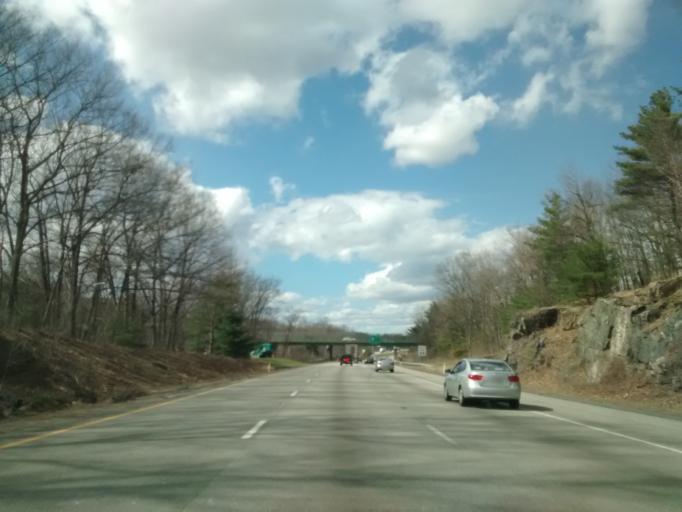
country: US
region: Massachusetts
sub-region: Middlesex County
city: Marlborough
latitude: 42.3308
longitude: -71.5744
